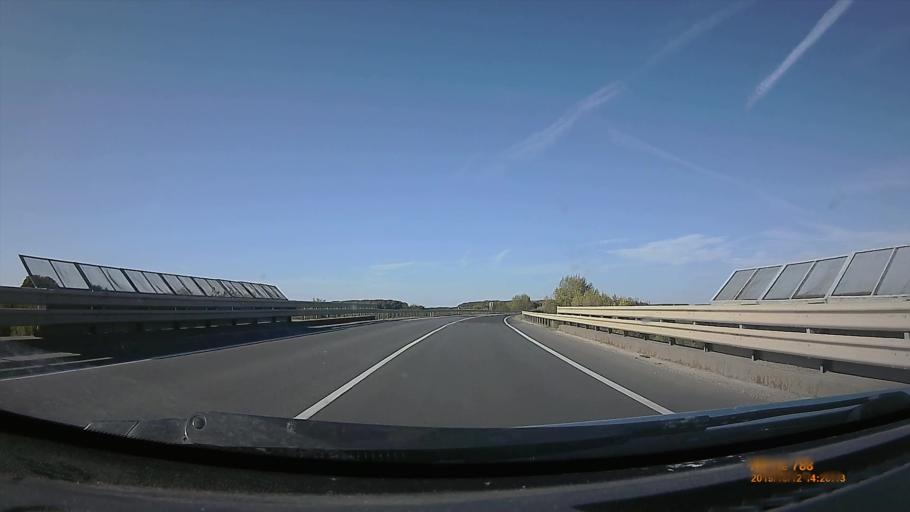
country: HU
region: Hajdu-Bihar
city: Biharkeresztes
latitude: 47.1322
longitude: 21.7430
